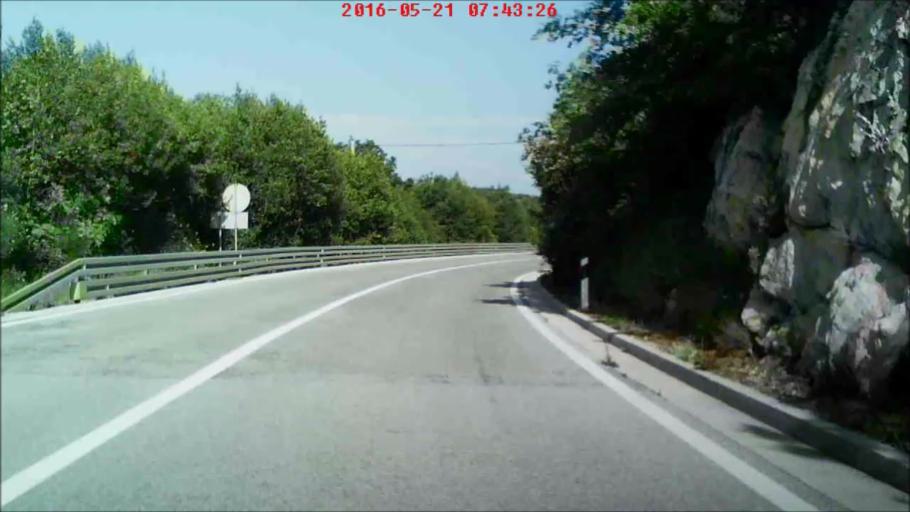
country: HR
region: Dubrovacko-Neretvanska
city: Podgora
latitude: 42.8131
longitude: 17.7897
